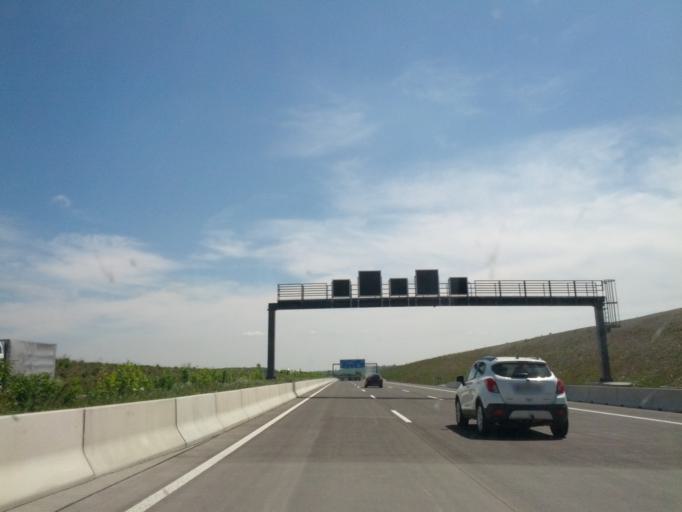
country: DE
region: Thuringia
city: Bucha
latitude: 50.8808
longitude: 11.4911
